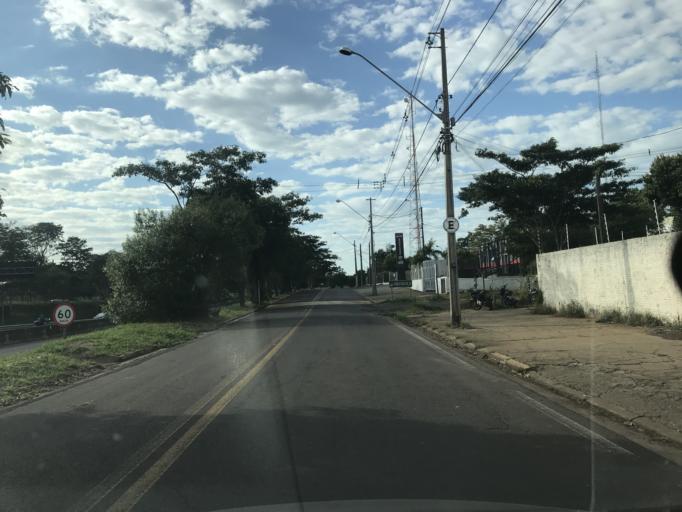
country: BR
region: Sao Paulo
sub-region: Presidente Prudente
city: Presidente Prudente
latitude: -22.1482
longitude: -51.3937
